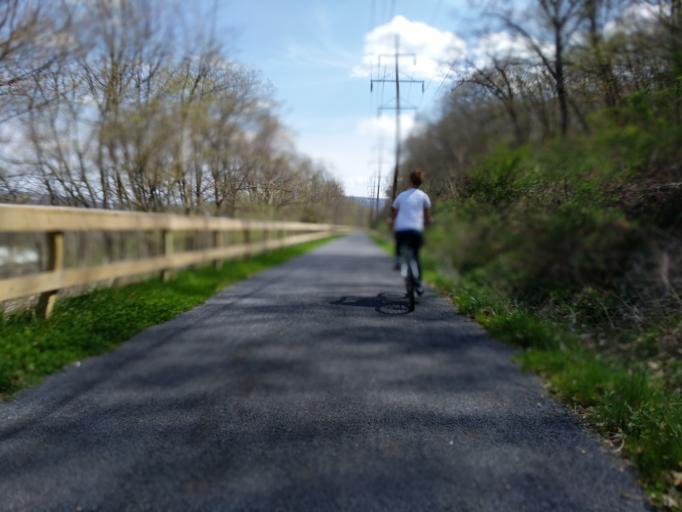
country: US
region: New York
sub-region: Tompkins County
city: Northwest Ithaca
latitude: 42.4560
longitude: -76.5190
